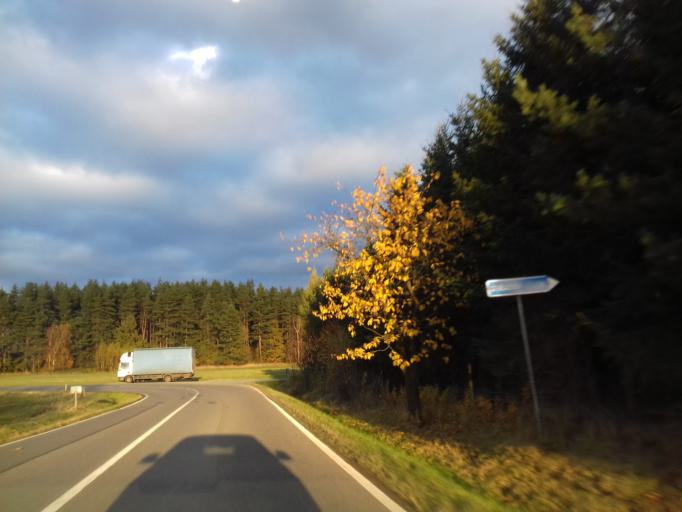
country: CZ
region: Pardubicky
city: Krouna
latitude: 49.8002
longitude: 16.0412
